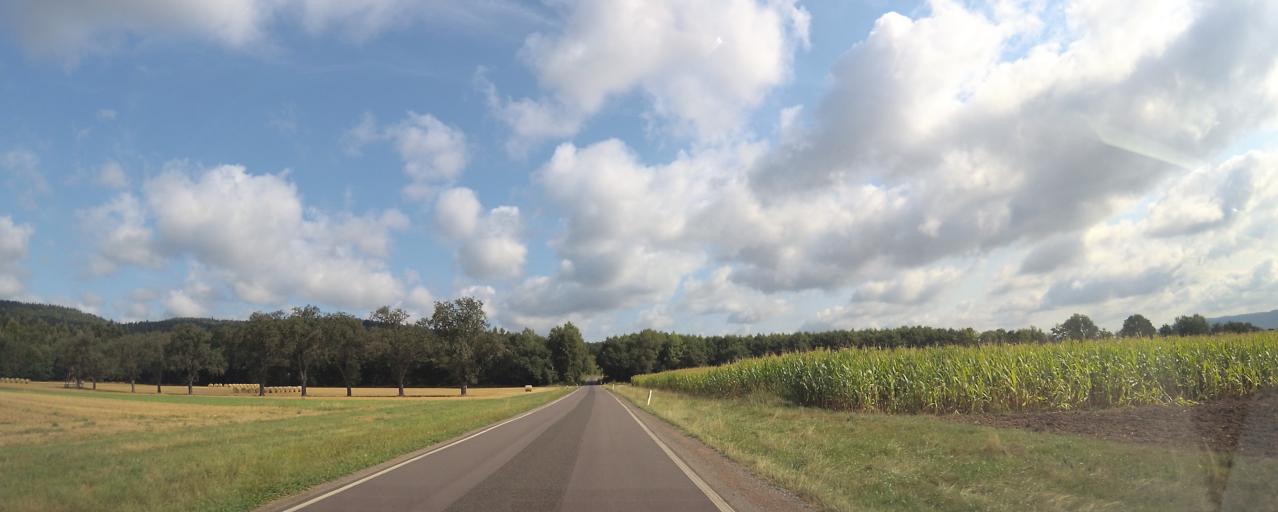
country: DE
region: Rheinland-Pfalz
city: Fohren
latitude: 49.8716
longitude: 6.7782
